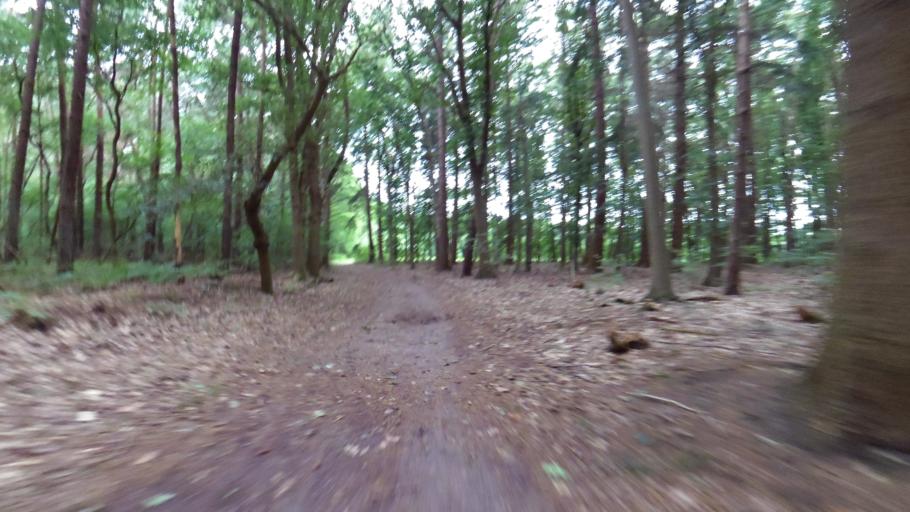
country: NL
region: Utrecht
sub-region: Gemeente Utrechtse Heuvelrug
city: Overberg
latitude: 52.0168
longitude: 5.5178
